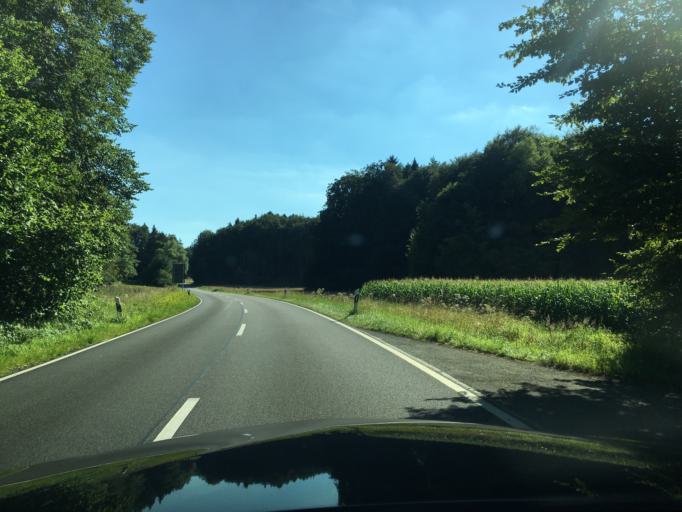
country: DE
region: Bavaria
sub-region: Upper Franconia
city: Hiltpoltstein
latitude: 49.6694
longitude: 11.3488
